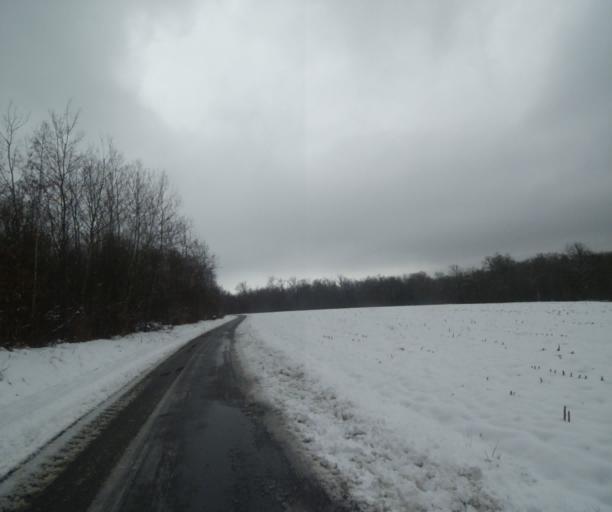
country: FR
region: Champagne-Ardenne
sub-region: Departement de la Haute-Marne
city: Laneuville-a-Remy
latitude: 48.4677
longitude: 4.8957
